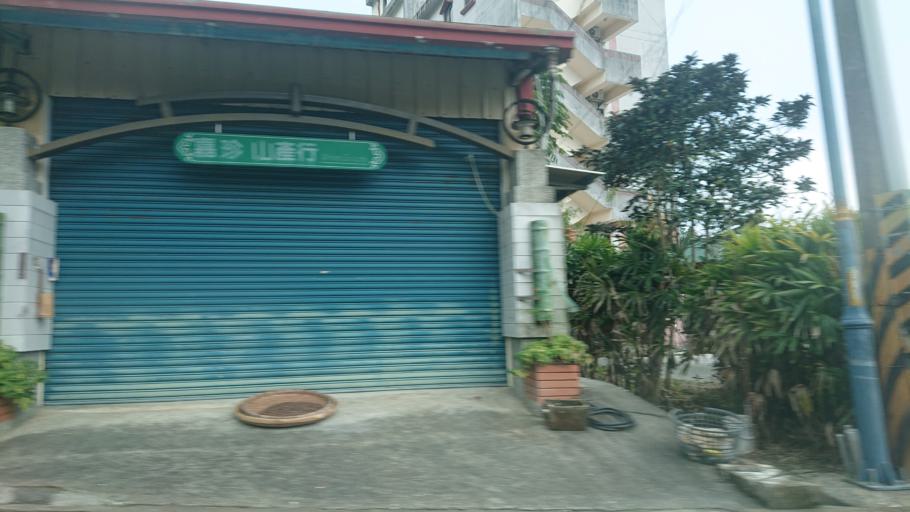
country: TW
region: Taiwan
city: Lugu
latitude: 23.5816
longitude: 120.6937
